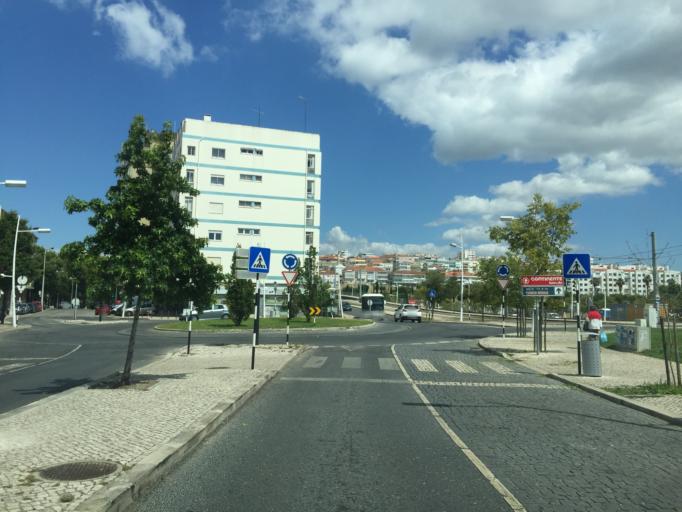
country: PT
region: Setubal
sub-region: Almada
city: Pragal
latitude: 38.6677
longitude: -9.1640
